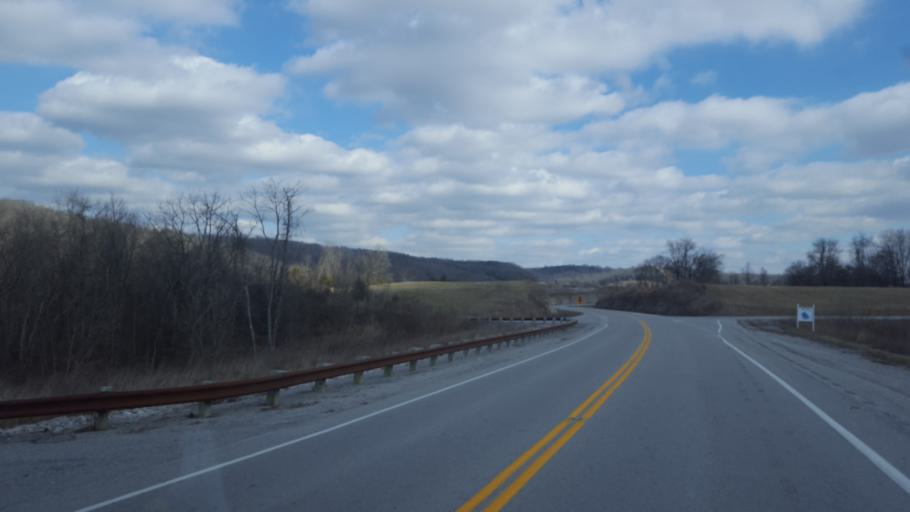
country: US
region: Kentucky
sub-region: Owen County
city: Owenton
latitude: 38.4718
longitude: -84.9530
